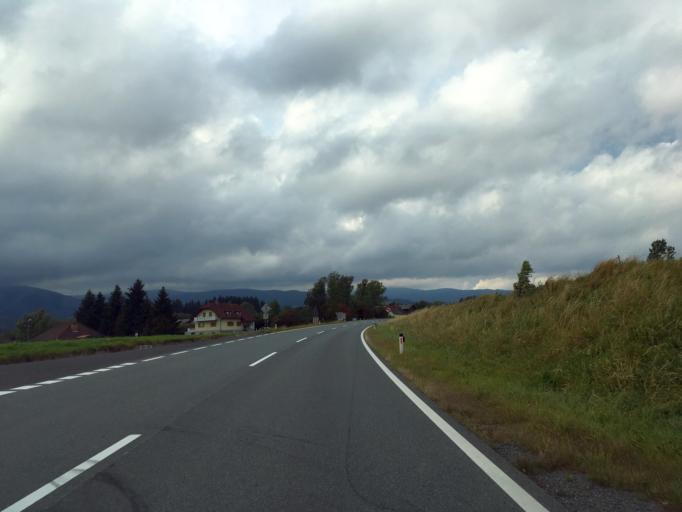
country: AT
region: Styria
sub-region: Politischer Bezirk Hartberg-Fuerstenfeld
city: Pinggau
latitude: 47.4578
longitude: 16.0653
